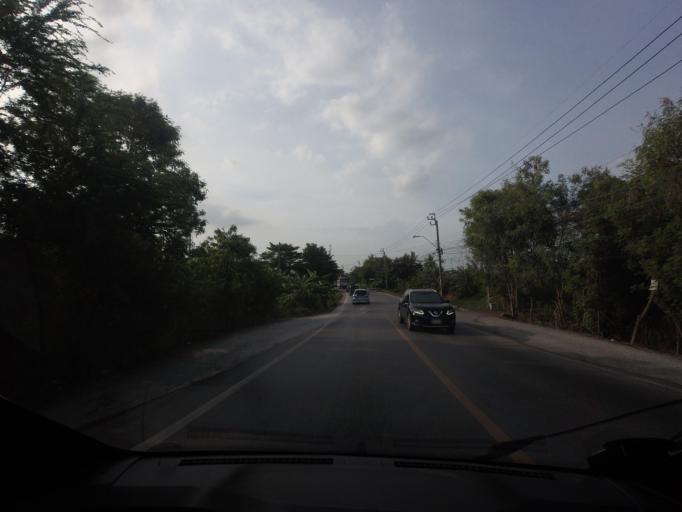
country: TH
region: Bangkok
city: Nong Chok
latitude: 13.8160
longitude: 100.8713
